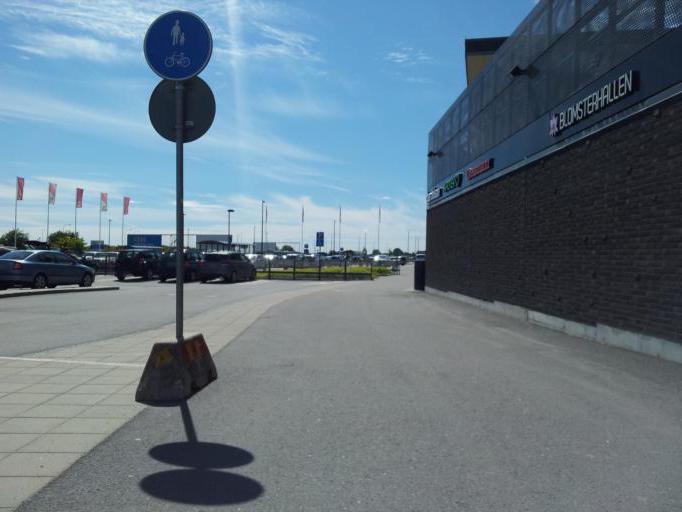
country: SE
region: Uppsala
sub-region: Uppsala Kommun
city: Uppsala
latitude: 59.8781
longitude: 17.6750
